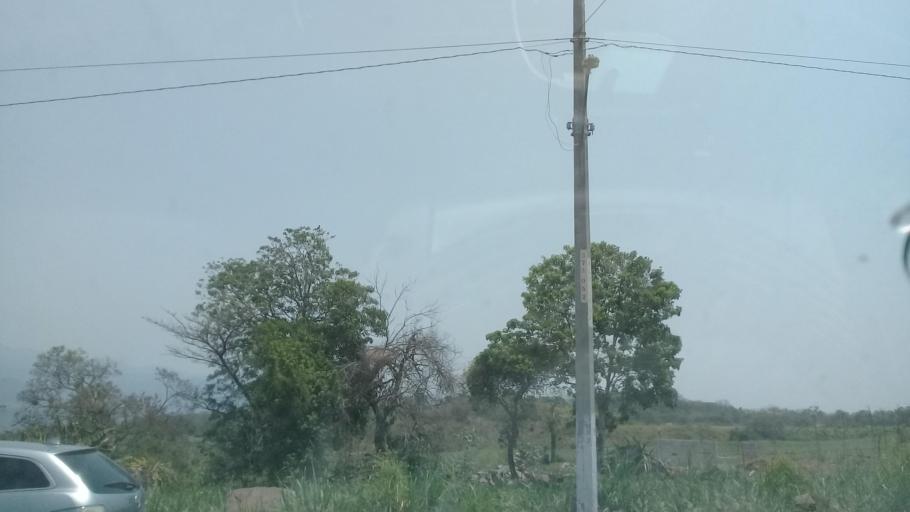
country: MX
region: Veracruz
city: El Castillo
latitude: 19.5670
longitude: -96.8475
